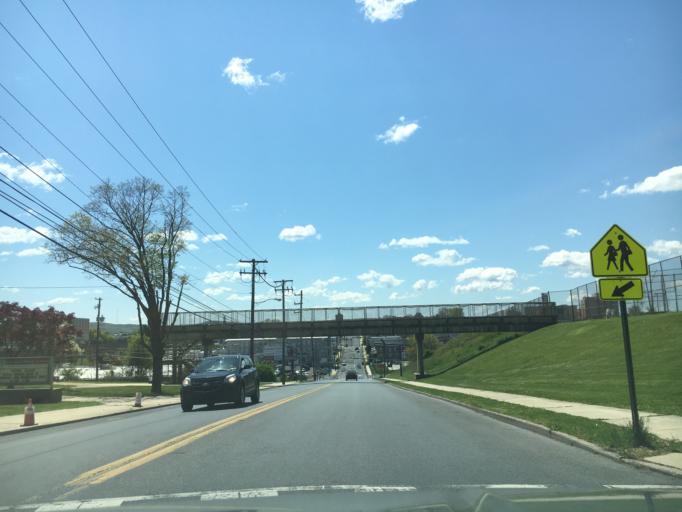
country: US
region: Pennsylvania
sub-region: Lehigh County
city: Allentown
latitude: 40.6106
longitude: -75.4942
